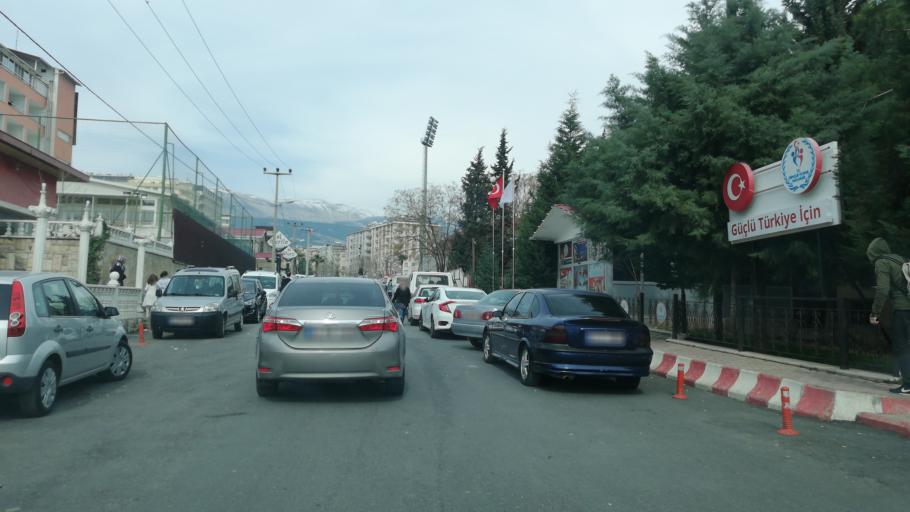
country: TR
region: Kahramanmaras
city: Kahramanmaras
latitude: 37.5735
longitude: 36.9218
